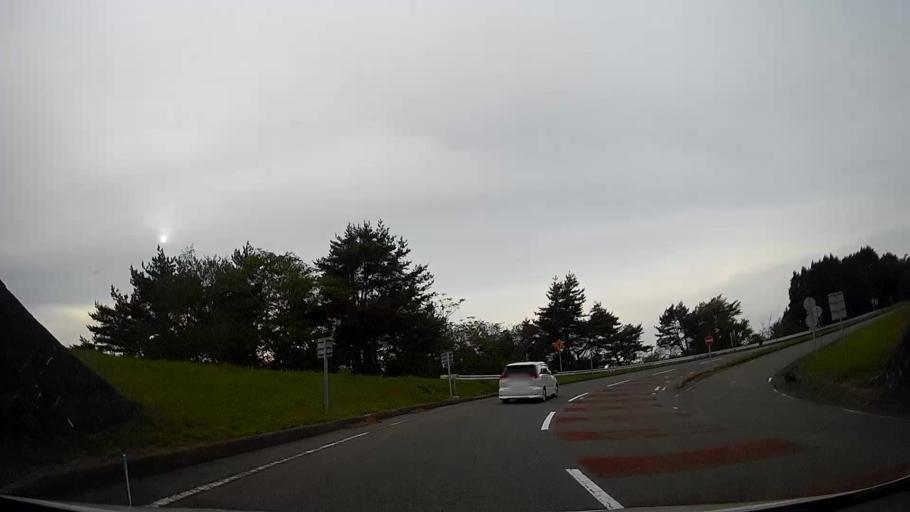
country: JP
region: Shizuoka
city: Atami
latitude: 35.0662
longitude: 139.0268
